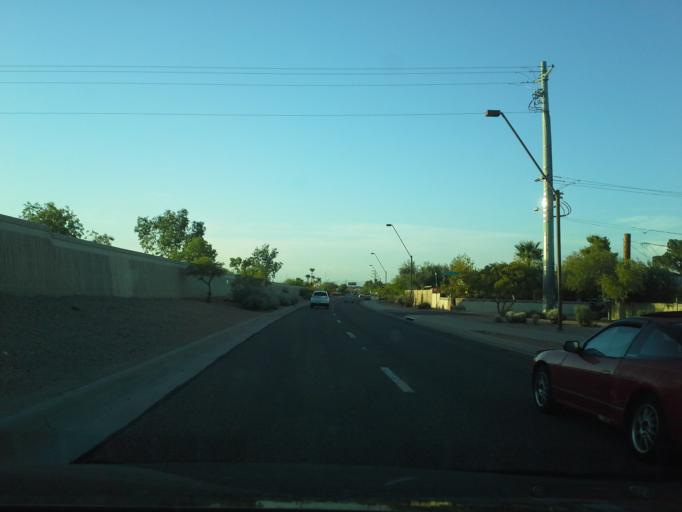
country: US
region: Arizona
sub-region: Maricopa County
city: Tempe
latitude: 33.4161
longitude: -111.8908
